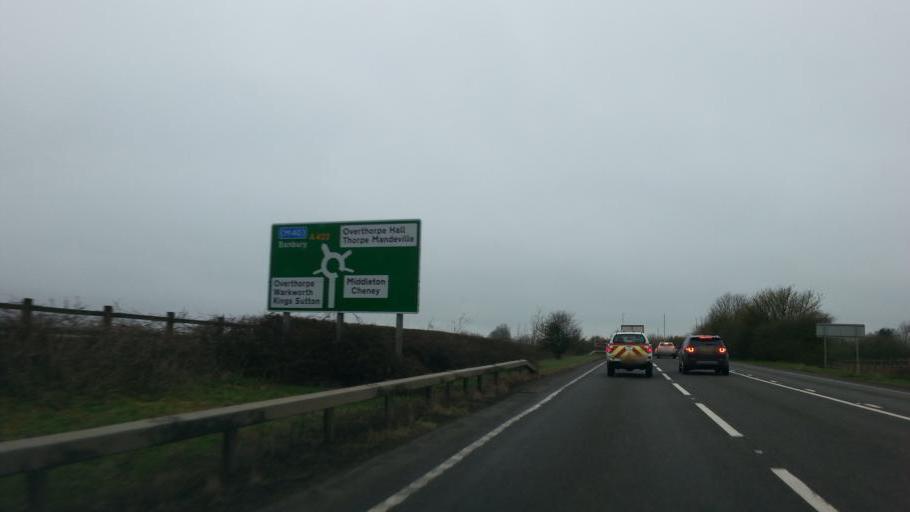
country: GB
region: England
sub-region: Oxfordshire
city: Banbury
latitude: 52.0712
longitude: -1.2855
